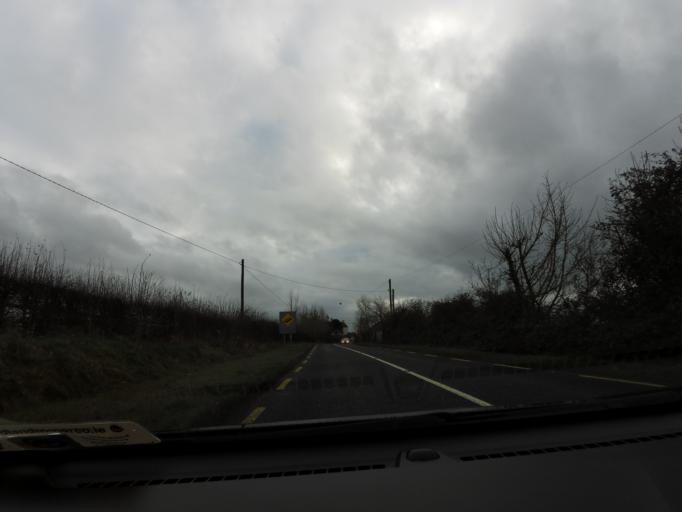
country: IE
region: Leinster
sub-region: Kilkenny
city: Kilkenny
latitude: 52.7094
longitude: -7.2791
